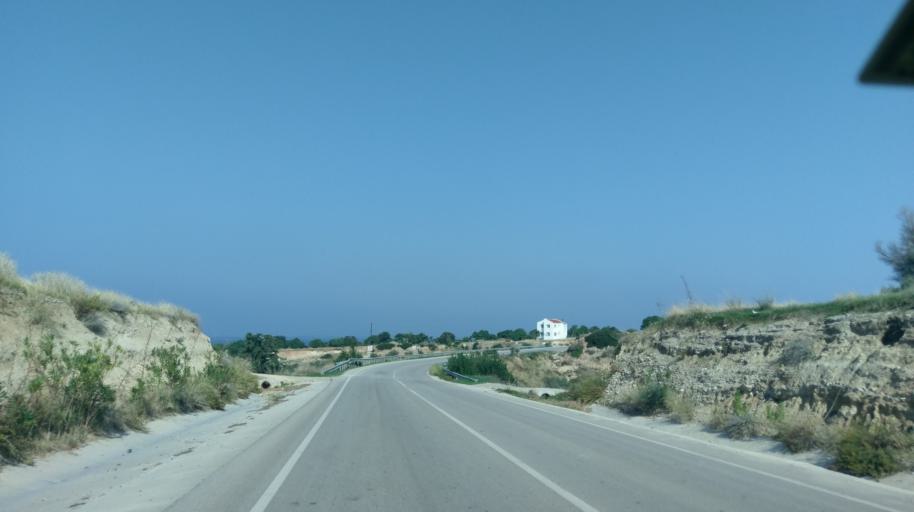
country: CY
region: Ammochostos
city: Lefkonoiko
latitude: 35.3813
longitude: 33.7200
